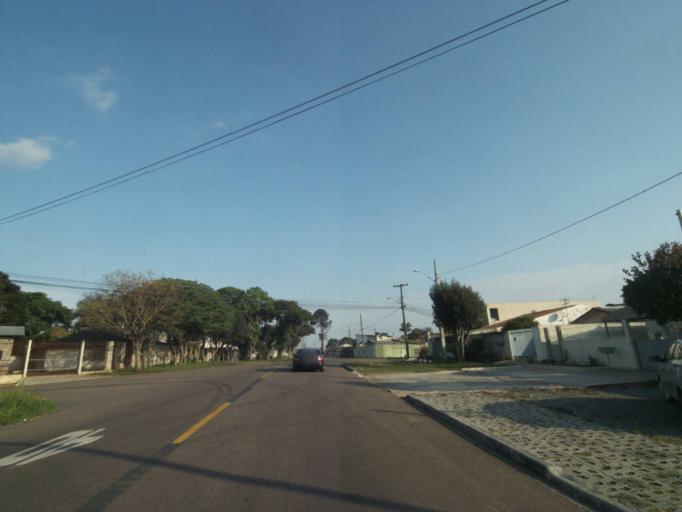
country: BR
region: Parana
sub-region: Curitiba
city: Curitiba
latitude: -25.4876
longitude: -49.3241
